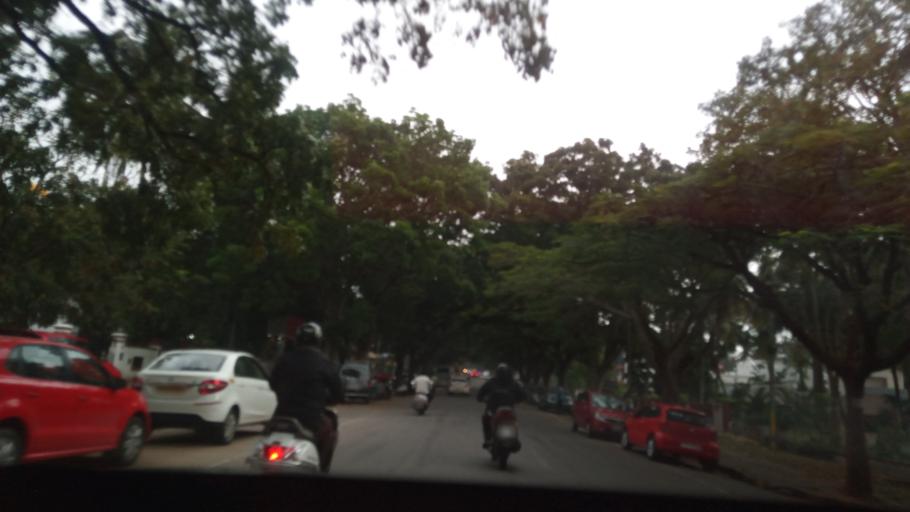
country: IN
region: Karnataka
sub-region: Mysore
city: Mysore
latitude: 12.3278
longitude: 76.6315
